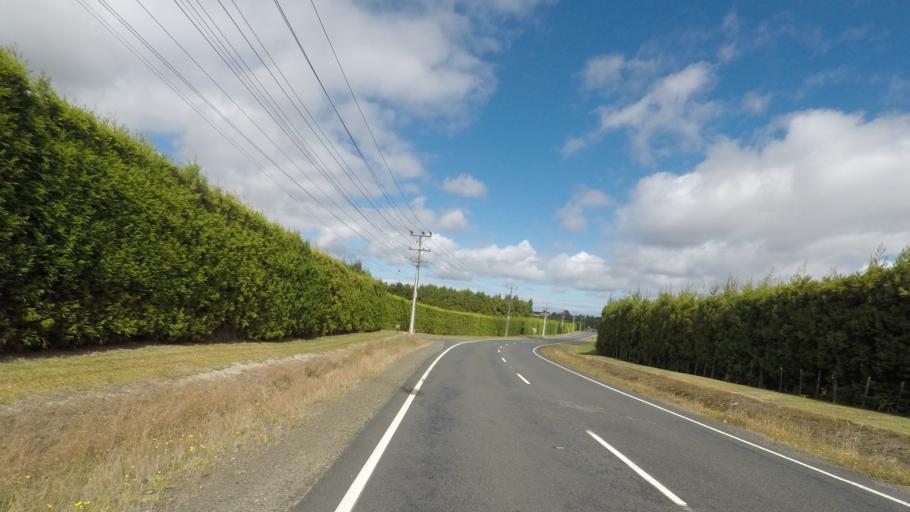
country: NZ
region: Auckland
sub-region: Auckland
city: Muriwai Beach
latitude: -36.7640
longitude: 174.5607
